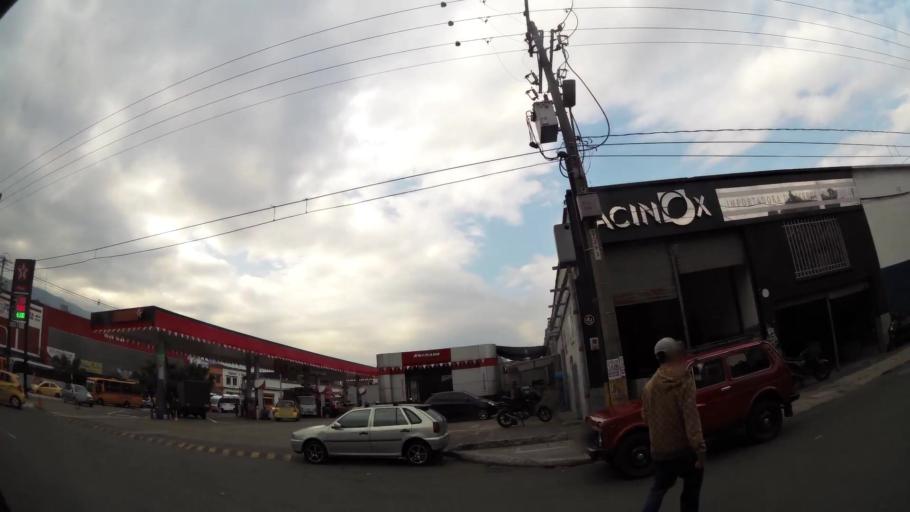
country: CO
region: Antioquia
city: Medellin
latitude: 6.2418
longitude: -75.5714
